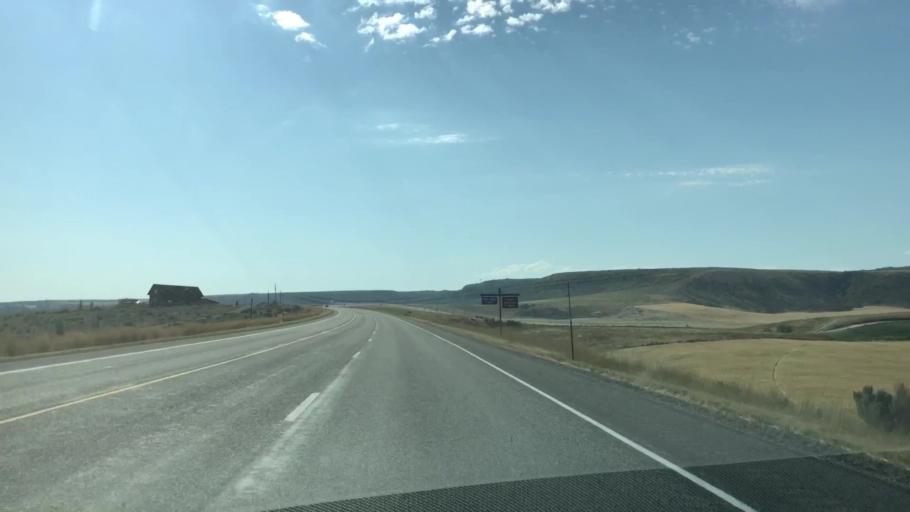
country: US
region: Idaho
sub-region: Madison County
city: Rexburg
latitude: 43.5960
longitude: -111.6446
